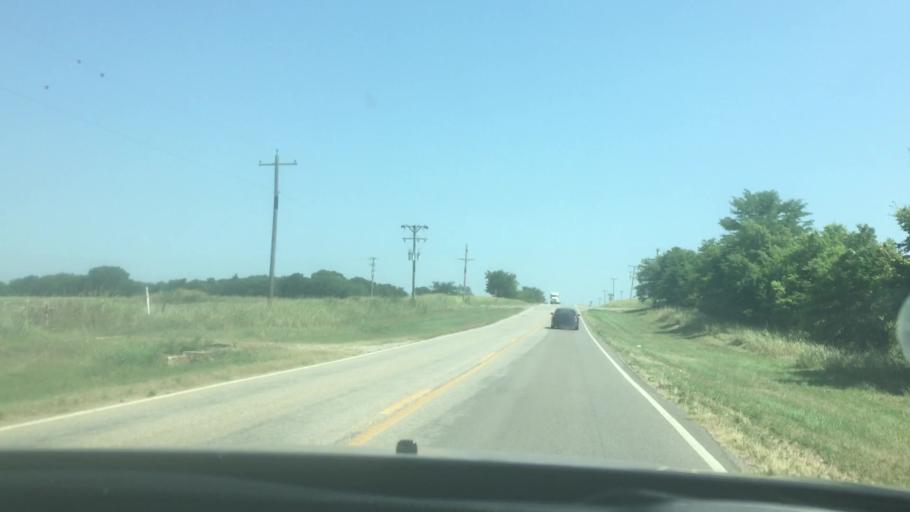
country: US
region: Oklahoma
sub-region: Coal County
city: Coalgate
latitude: 34.4169
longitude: -96.4245
